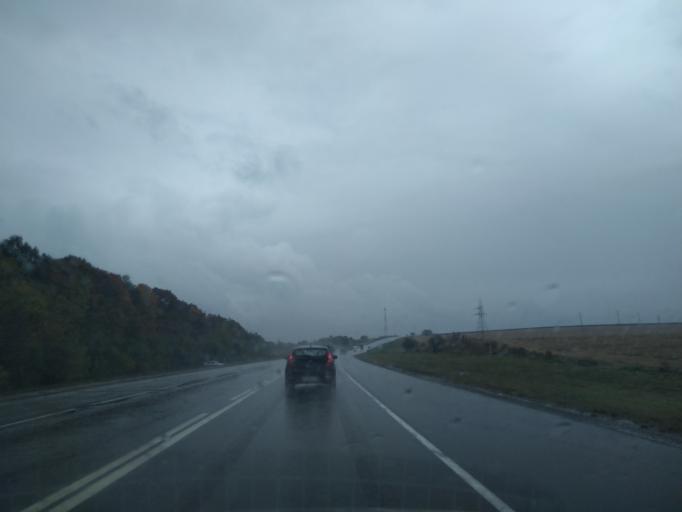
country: RU
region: Tula
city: Shchekino
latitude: 53.9630
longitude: 37.4833
